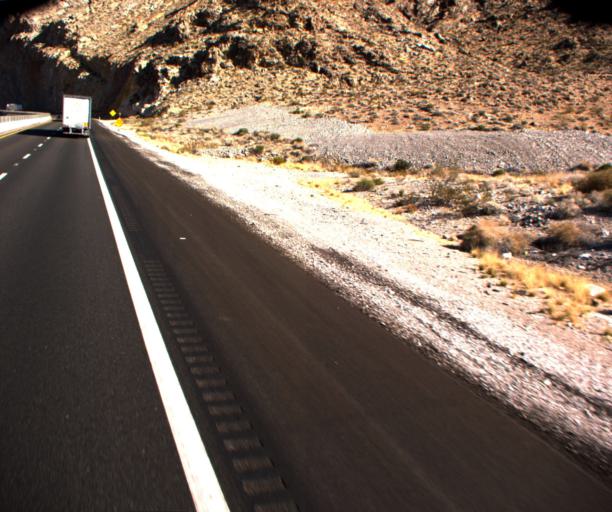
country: US
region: Arizona
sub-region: Mohave County
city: Beaver Dam
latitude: 36.9180
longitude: -113.8671
